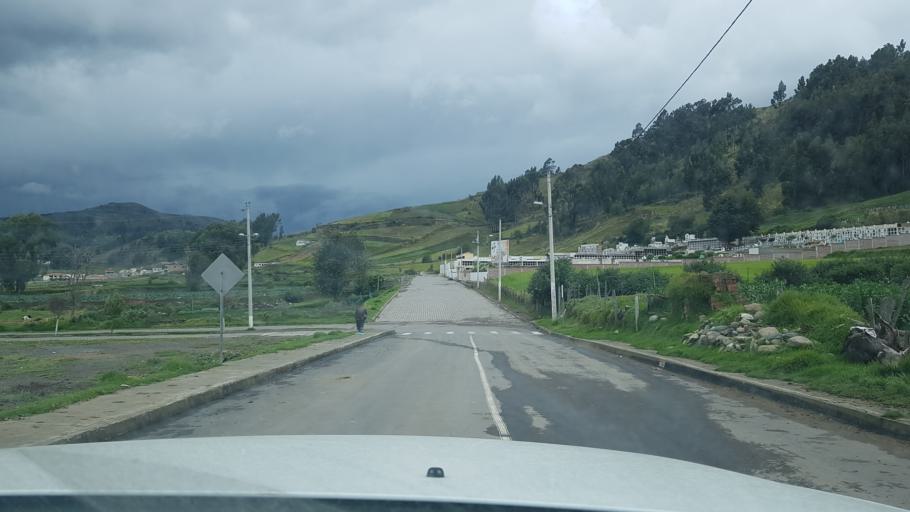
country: EC
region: Chimborazo
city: Riobamba
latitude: -1.7050
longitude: -78.7766
